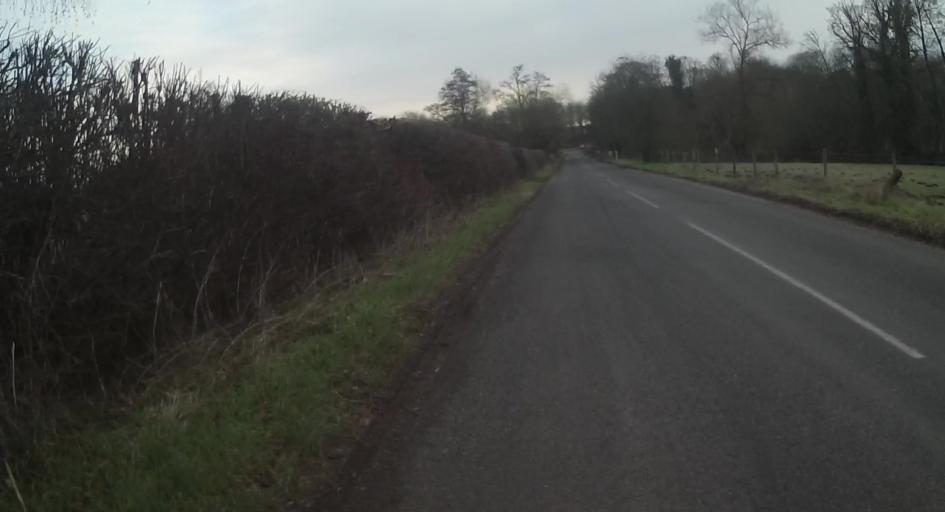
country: GB
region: England
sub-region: Hampshire
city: Highclere
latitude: 51.2243
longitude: -1.3783
